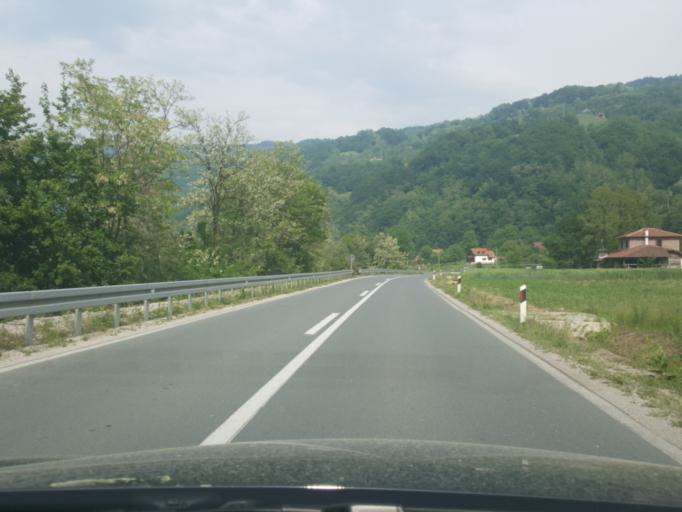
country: RS
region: Central Serbia
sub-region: Zlatiborski Okrug
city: Bajina Basta
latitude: 44.0117
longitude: 19.6125
